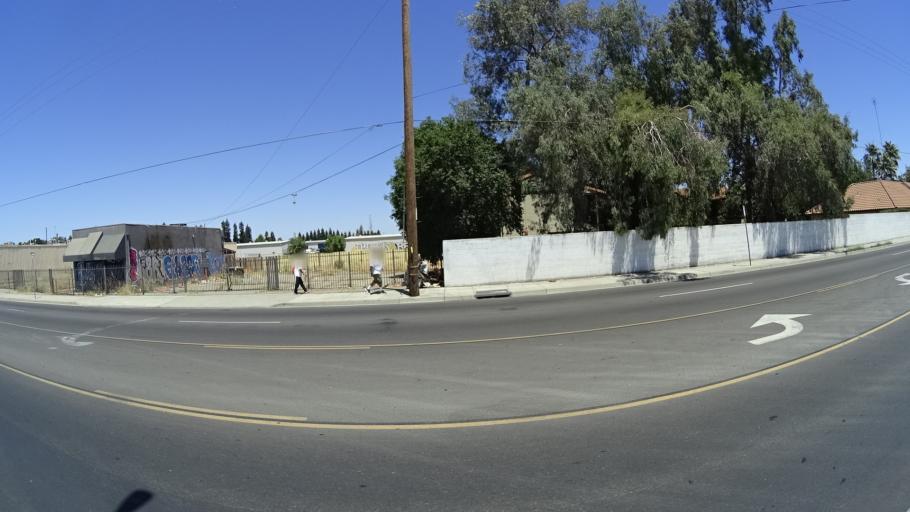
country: US
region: California
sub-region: Fresno County
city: West Park
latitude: 36.7719
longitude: -119.8430
